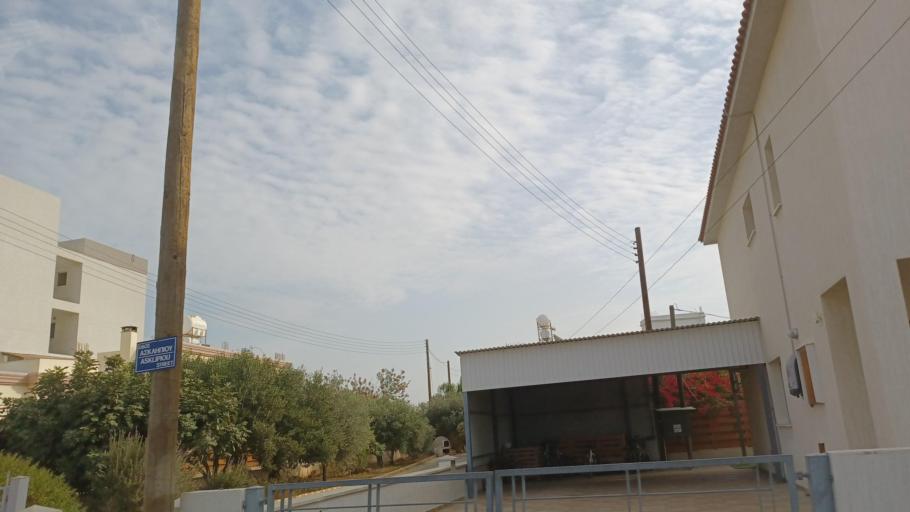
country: CY
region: Limassol
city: Ypsonas
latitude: 34.6980
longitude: 32.9569
